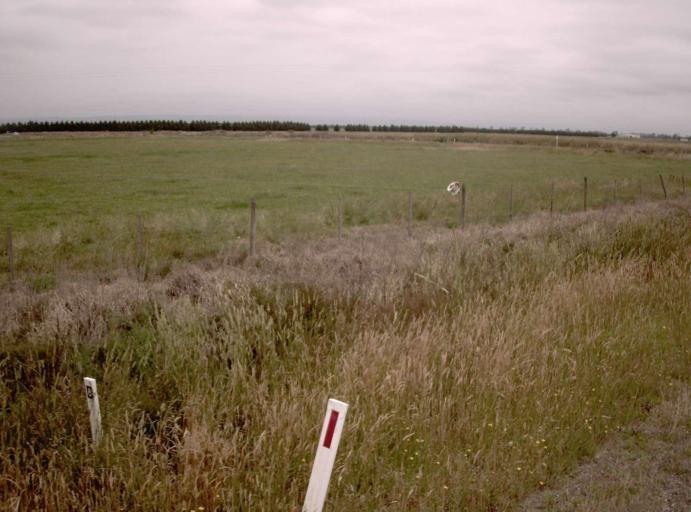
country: AU
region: Victoria
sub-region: Wellington
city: Heyfield
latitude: -38.0904
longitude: 146.7723
